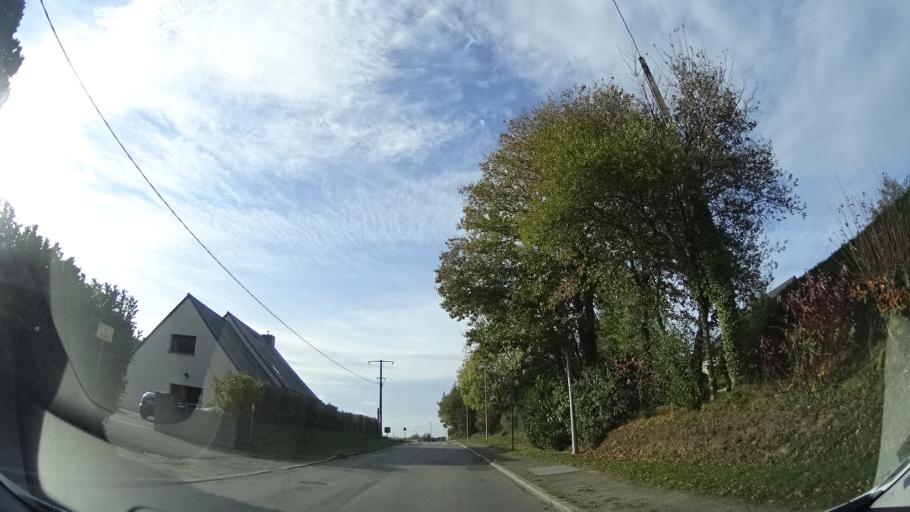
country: FR
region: Brittany
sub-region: Departement d'Ille-et-Vilaine
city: Romille
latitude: 48.2153
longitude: -1.9027
